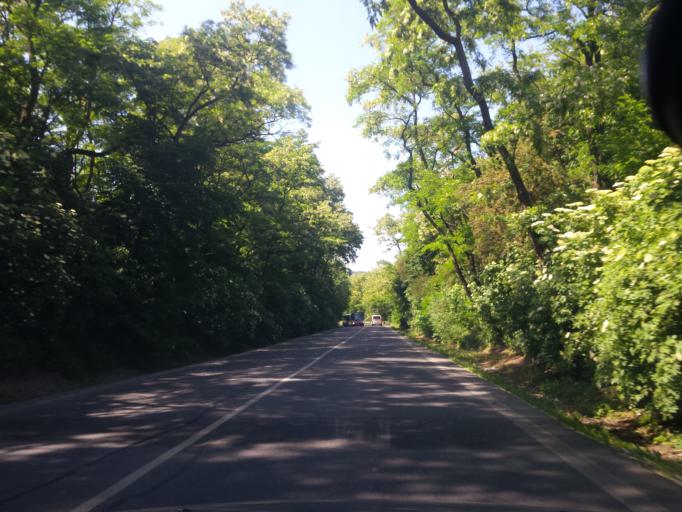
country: CZ
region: Central Bohemia
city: Horomerice
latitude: 50.1009
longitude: 14.3625
